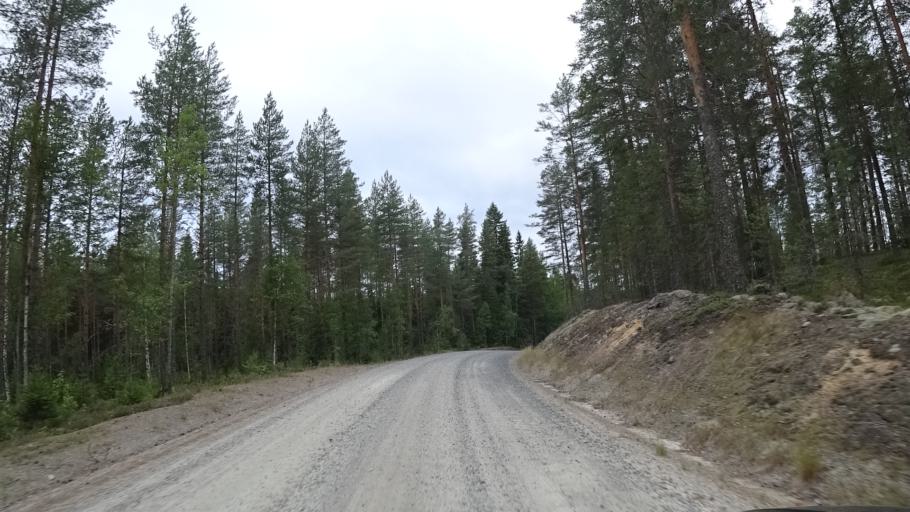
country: FI
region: North Karelia
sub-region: Pielisen Karjala
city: Lieksa
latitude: 63.2390
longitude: 30.3522
